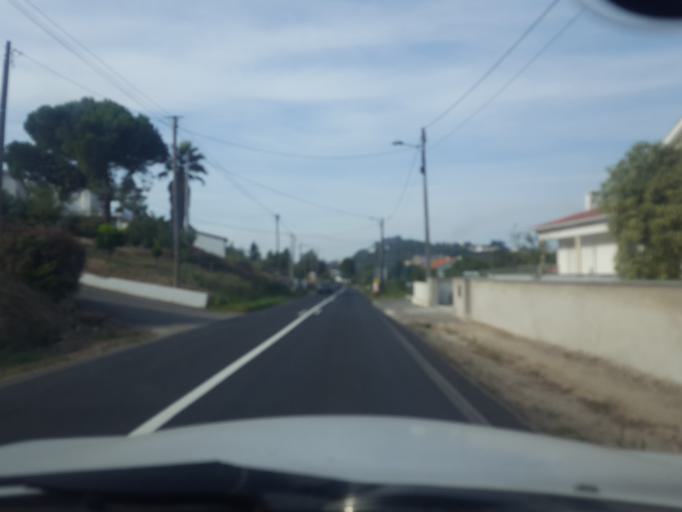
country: PT
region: Leiria
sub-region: Leiria
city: Leiria
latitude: 39.7151
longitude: -8.7889
